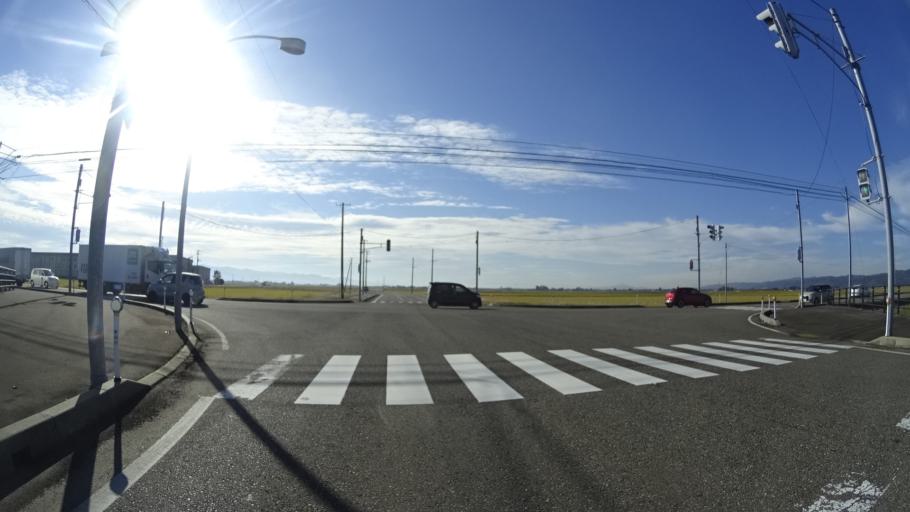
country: JP
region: Niigata
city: Mitsuke
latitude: 37.5553
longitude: 138.8492
